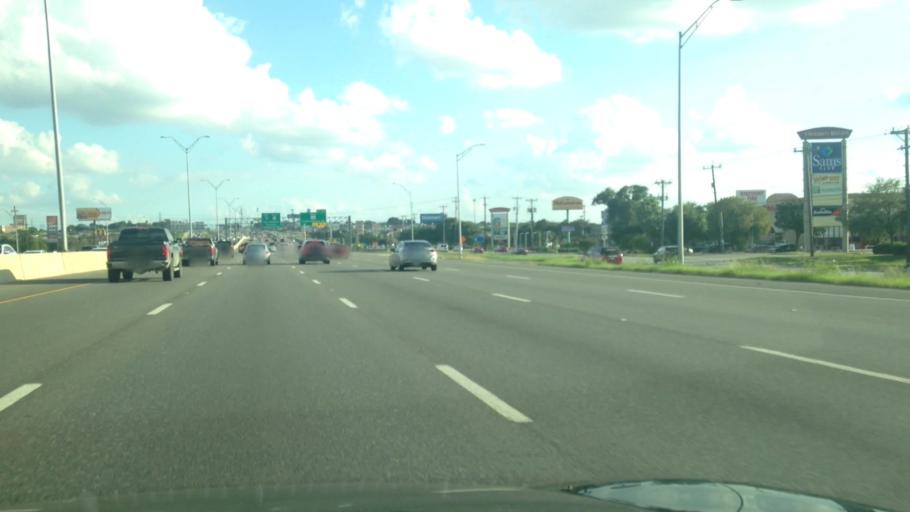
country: US
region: Texas
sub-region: Bexar County
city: Shavano Park
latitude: 29.5685
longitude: -98.5934
